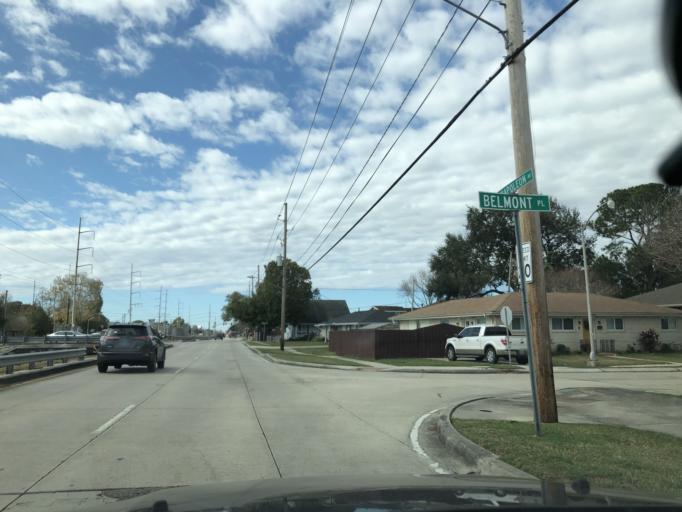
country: US
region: Louisiana
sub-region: Jefferson Parish
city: Metairie Terrace
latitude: 29.9931
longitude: -90.1685
